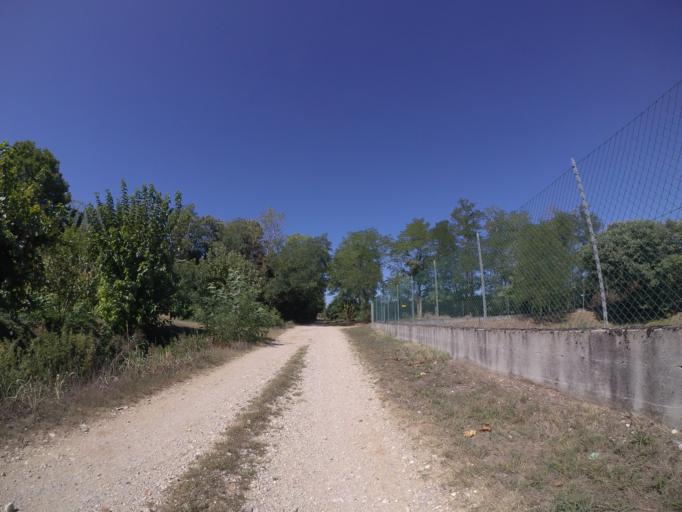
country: IT
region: Friuli Venezia Giulia
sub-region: Provincia di Udine
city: Bertiolo
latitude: 45.9503
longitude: 13.0847
